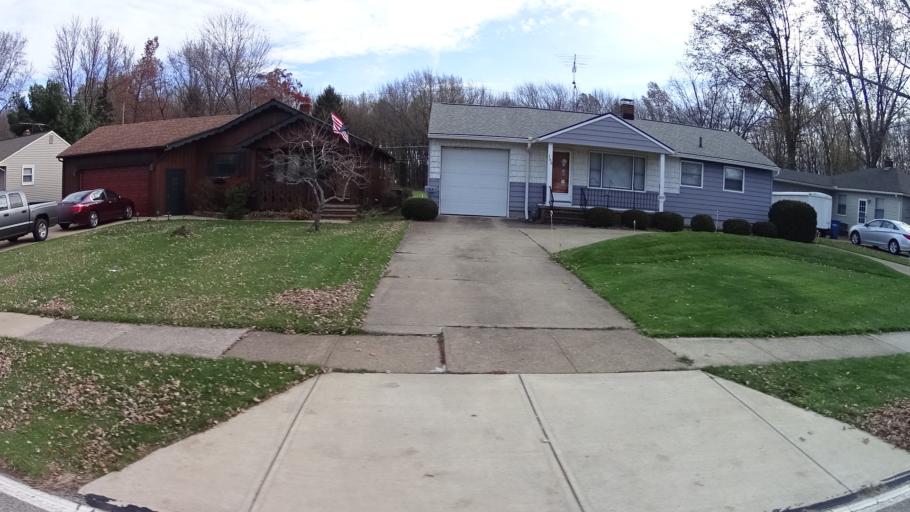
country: US
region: Ohio
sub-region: Lorain County
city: Avon Lake
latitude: 41.4979
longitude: -82.0616
